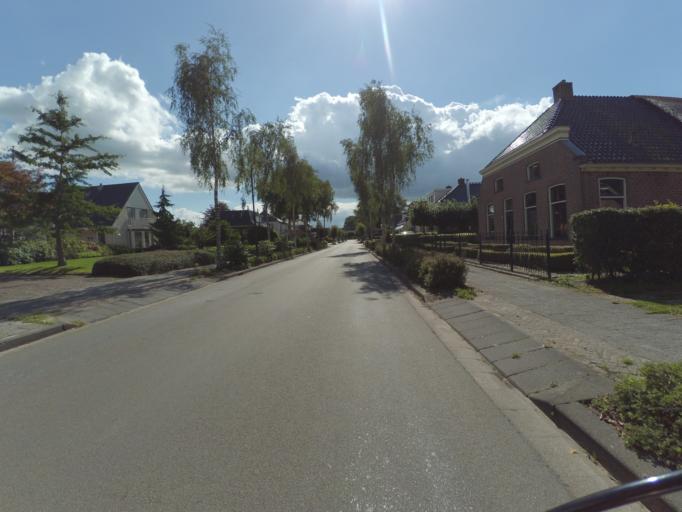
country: NL
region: Friesland
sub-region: Gemeente Achtkarspelen
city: Drogeham
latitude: 53.2036
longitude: 6.1097
